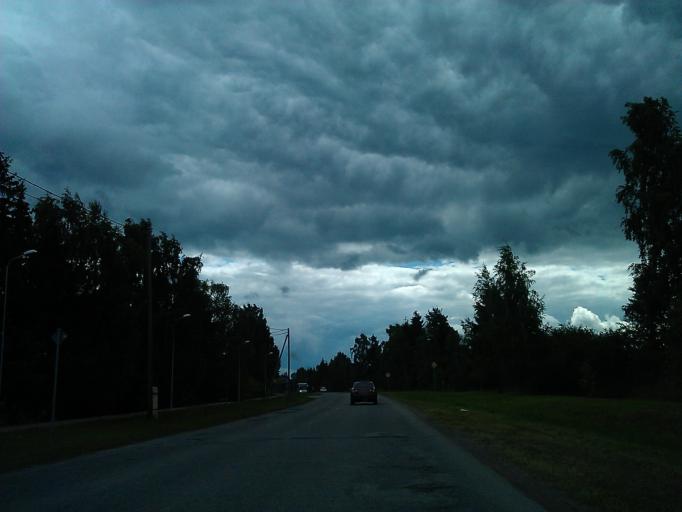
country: LV
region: Dobeles Rajons
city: Dobele
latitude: 56.6332
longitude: 23.2612
